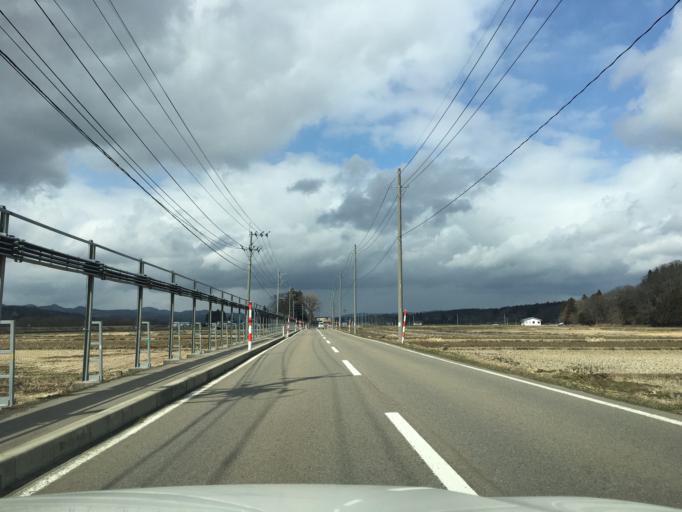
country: JP
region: Akita
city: Takanosu
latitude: 40.1316
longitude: 140.3588
